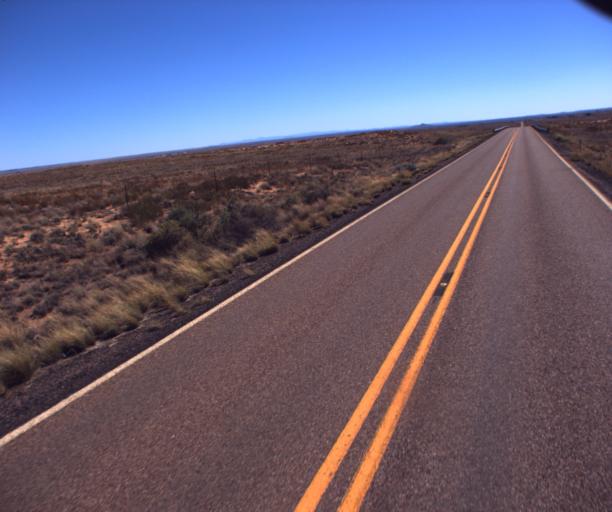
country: US
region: Arizona
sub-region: Navajo County
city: Holbrook
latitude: 35.0056
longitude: -110.0897
